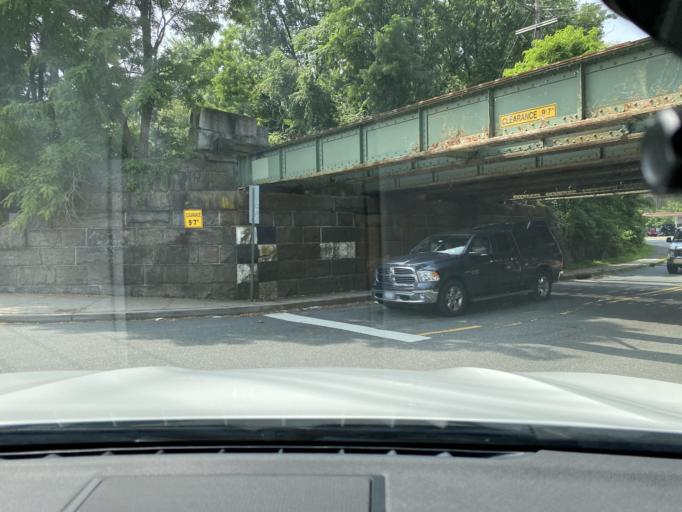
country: US
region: New York
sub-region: Rockland County
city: Suffern
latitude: 41.1071
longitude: -74.1499
